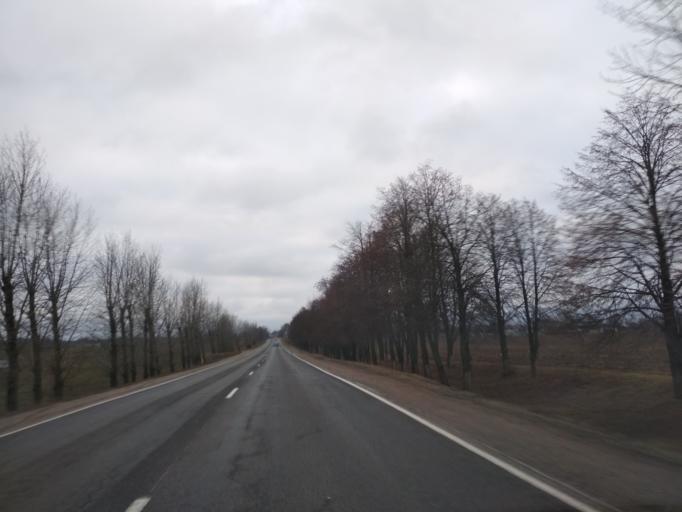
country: BY
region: Minsk
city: Blon'
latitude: 53.5317
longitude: 28.1515
